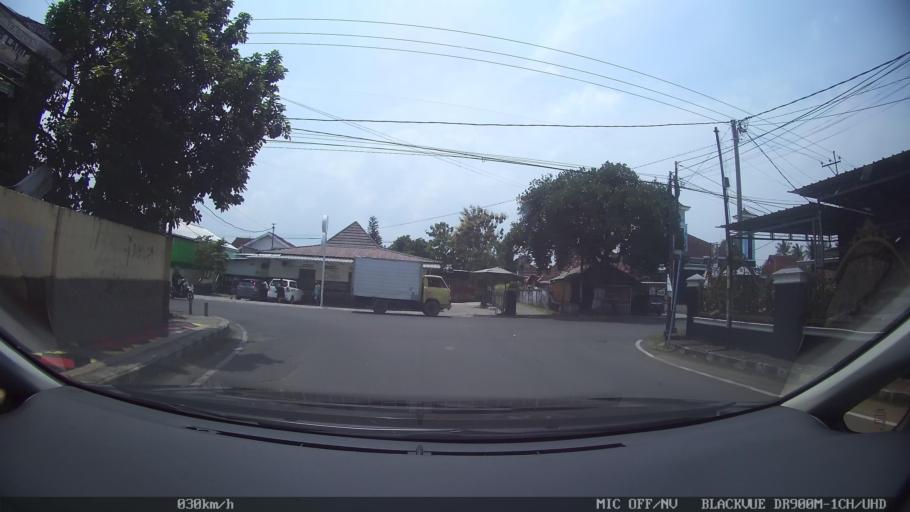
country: ID
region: Lampung
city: Bandarlampung
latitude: -5.4179
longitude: 105.2621
